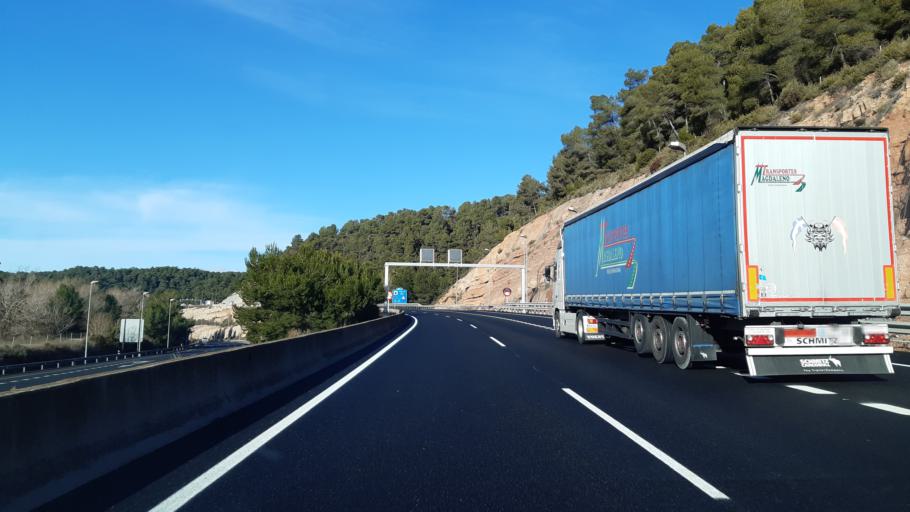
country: ES
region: Catalonia
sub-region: Provincia de Barcelona
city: Castelloli
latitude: 41.5945
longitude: 1.7487
